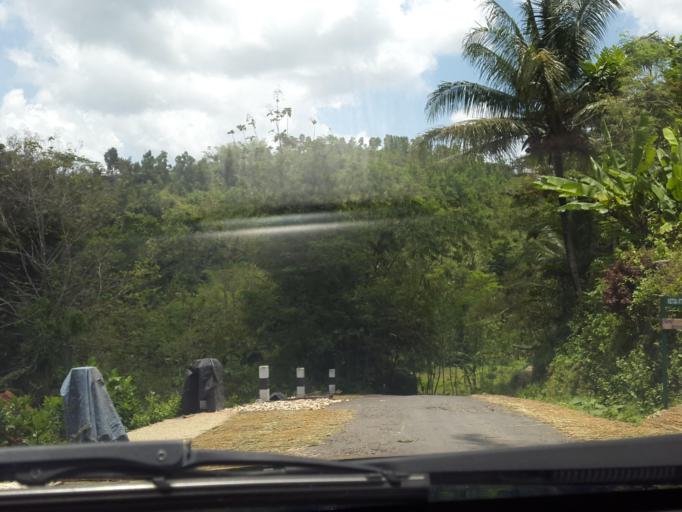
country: ID
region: Daerah Istimewa Yogyakarta
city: Wonosari
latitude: -7.9030
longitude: 110.7492
